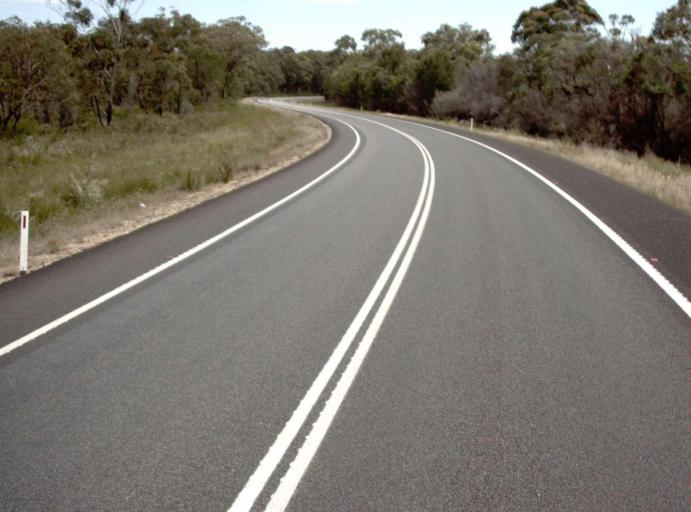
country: AU
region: New South Wales
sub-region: Bega Valley
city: Eden
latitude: -37.5174
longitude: 149.4978
